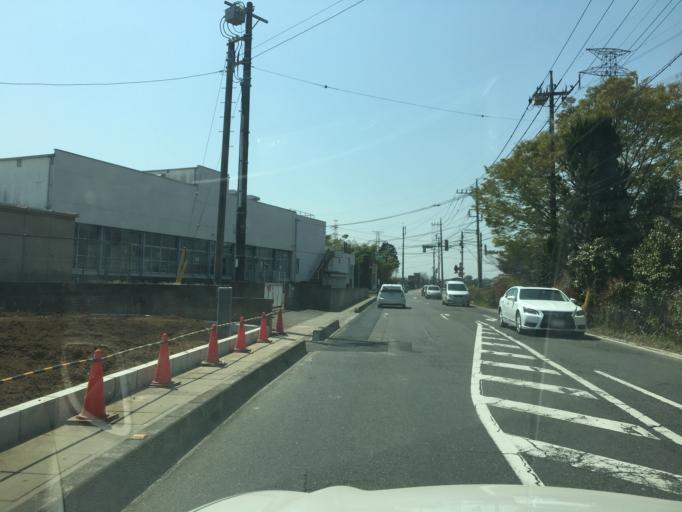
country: JP
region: Saitama
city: Sayama
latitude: 35.8461
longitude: 139.4471
